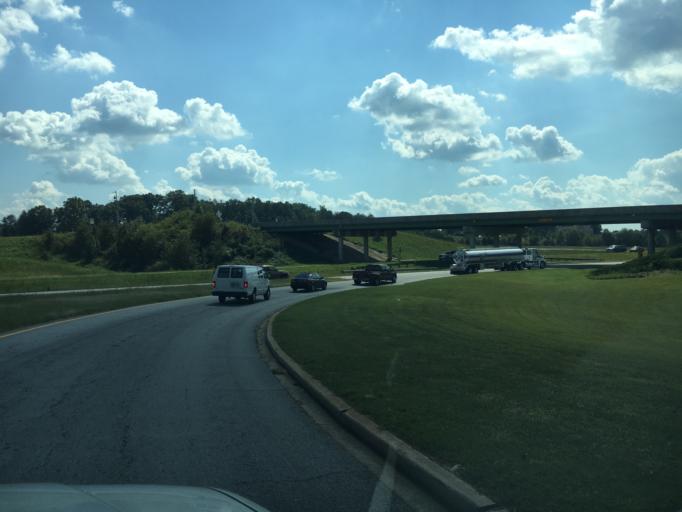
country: US
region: South Carolina
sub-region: Anderson County
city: Powdersville
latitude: 34.8293
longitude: -82.5281
